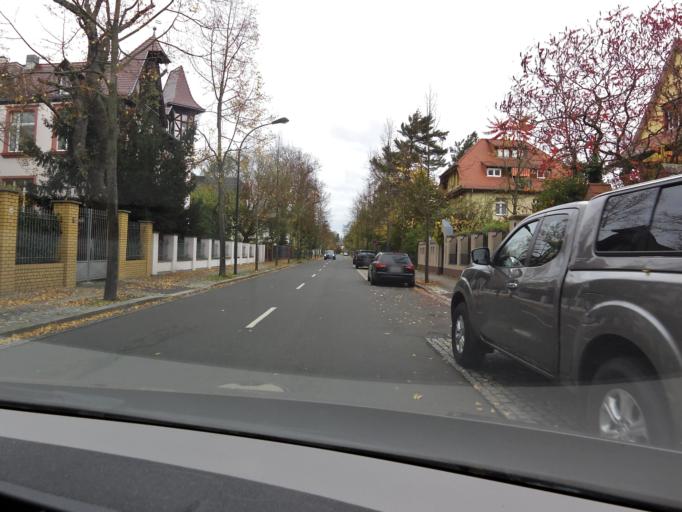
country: DE
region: Saxony
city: Markkleeberg
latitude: 51.2838
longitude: 12.3736
